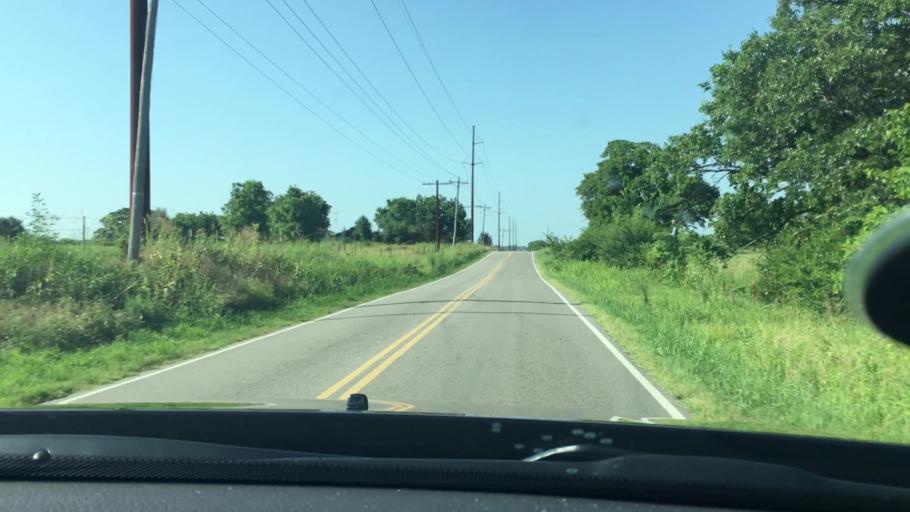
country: US
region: Oklahoma
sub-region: Pontotoc County
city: Ada
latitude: 34.8031
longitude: -96.6348
